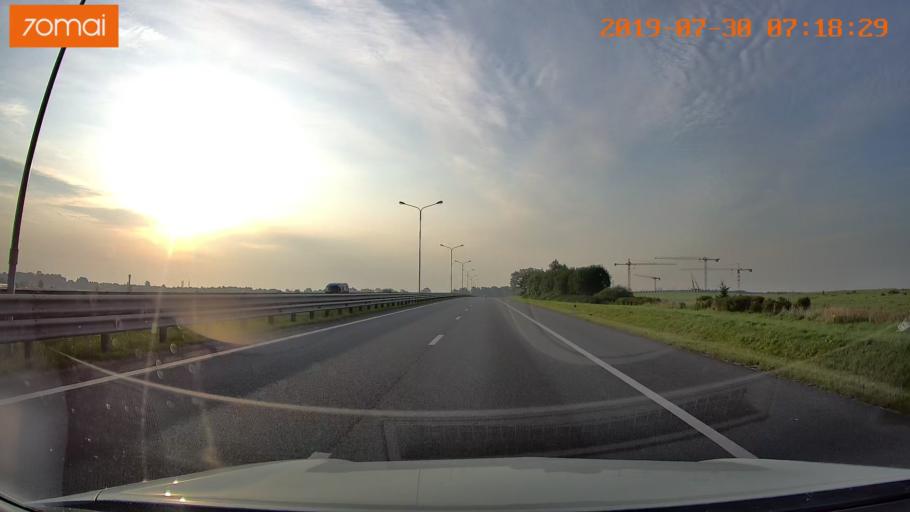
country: RU
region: Kaliningrad
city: Bol'shoe Isakovo
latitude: 54.7038
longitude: 20.6495
